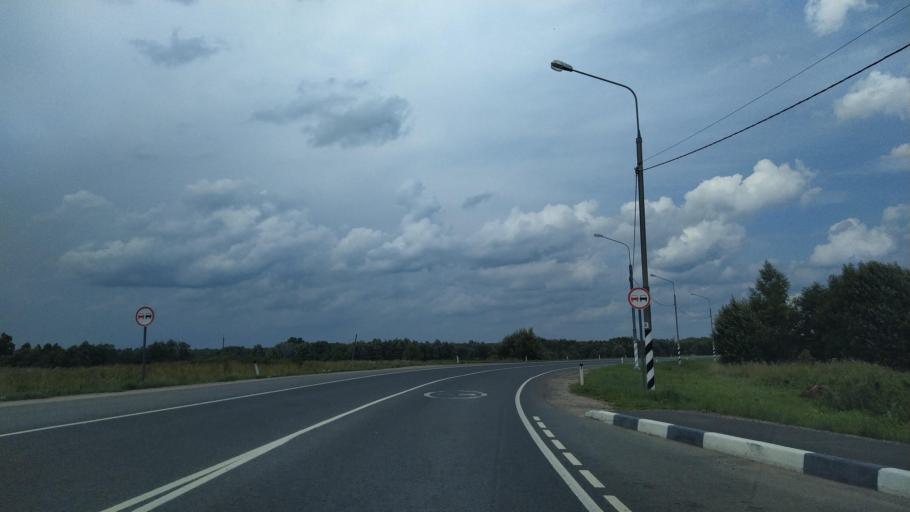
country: RU
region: Pskov
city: Dno
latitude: 58.0573
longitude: 29.9662
